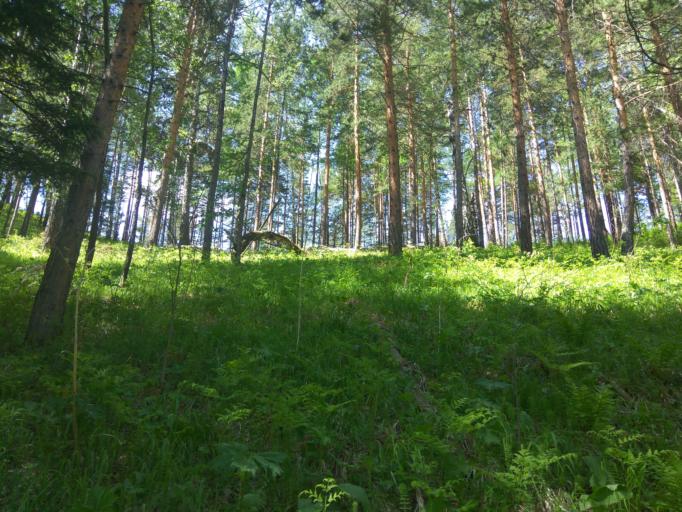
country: RU
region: Krasnoyarskiy
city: Krasnoyarsk
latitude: 55.9028
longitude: 92.9390
